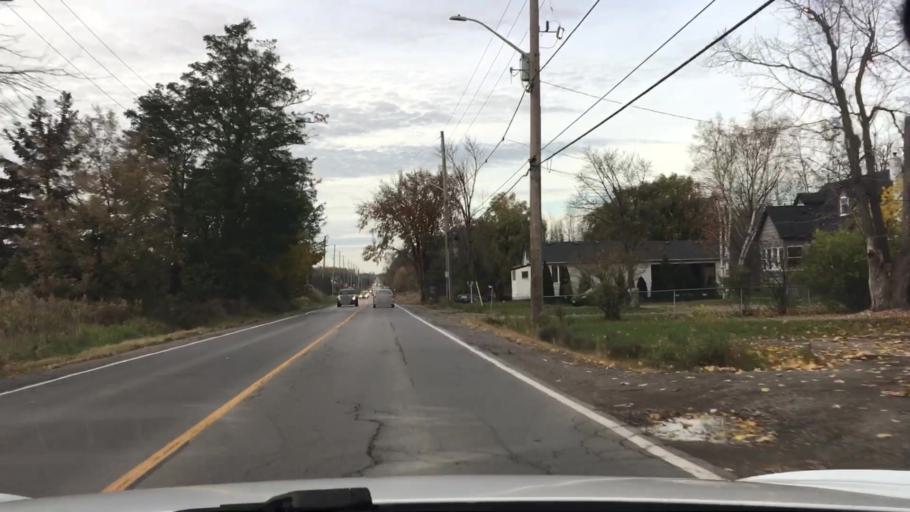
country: CA
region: Ontario
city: Oshawa
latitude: 43.9192
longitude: -78.8189
